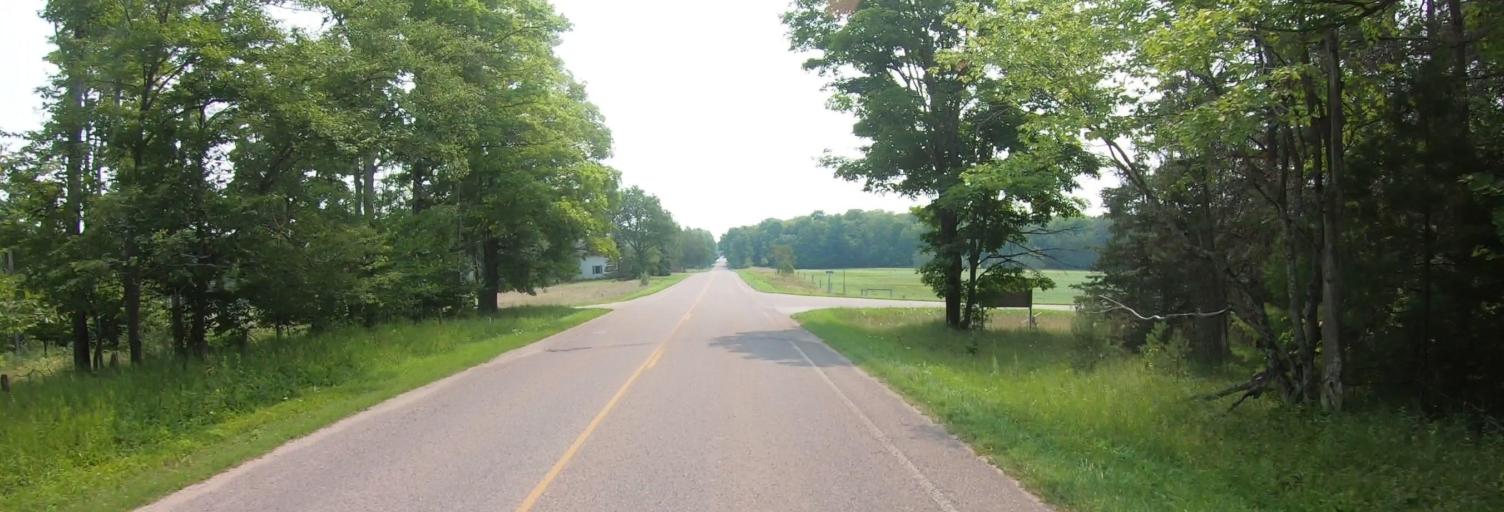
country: CA
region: Ontario
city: Thessalon
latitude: 46.0064
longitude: -83.7385
